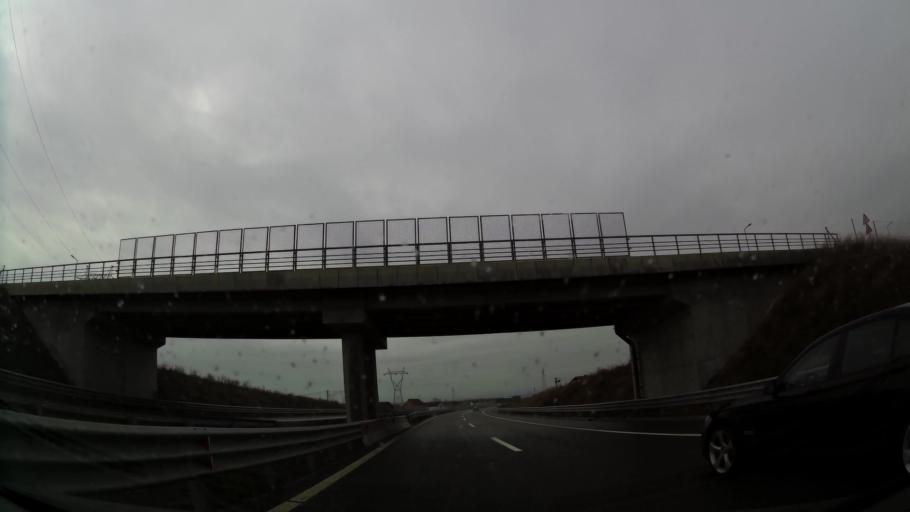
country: XK
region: Pristina
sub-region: Lipjan
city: Lipljan
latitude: 42.4712
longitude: 21.1810
